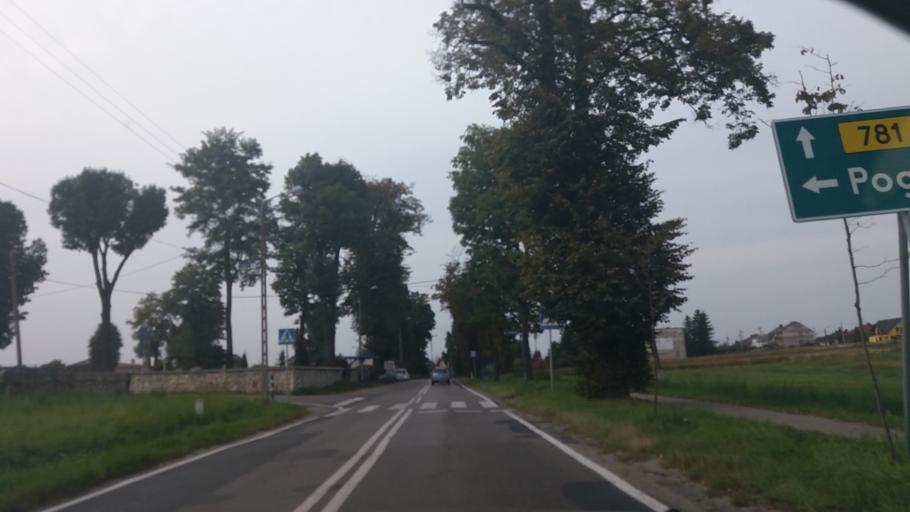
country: PL
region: Lesser Poland Voivodeship
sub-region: Powiat chrzanowski
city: Plaza
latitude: 50.1000
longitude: 19.4619
